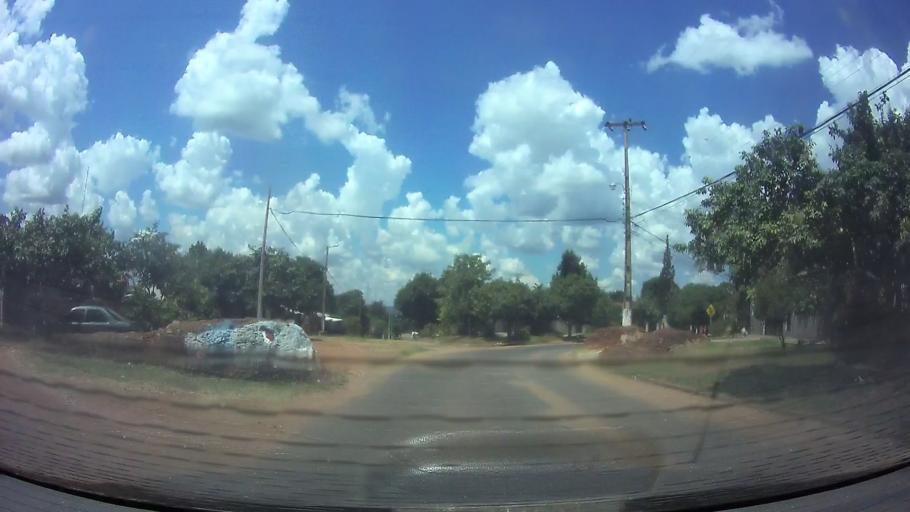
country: PY
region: Central
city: Limpio
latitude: -25.1672
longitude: -57.4430
